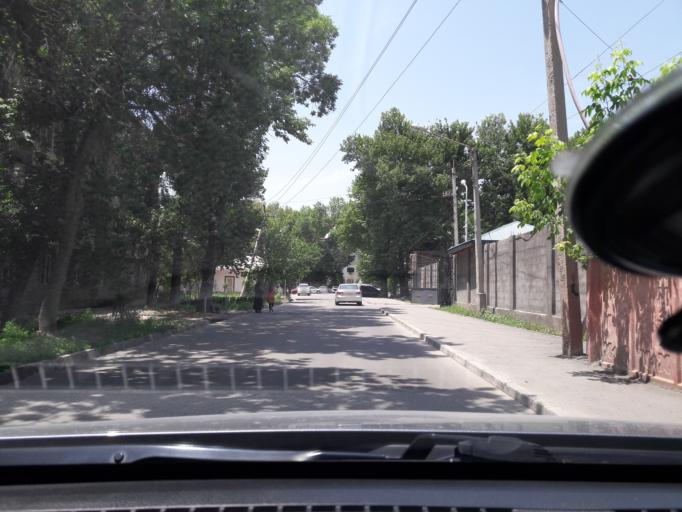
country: TJ
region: Dushanbe
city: Dushanbe
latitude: 38.5891
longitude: 68.7533
